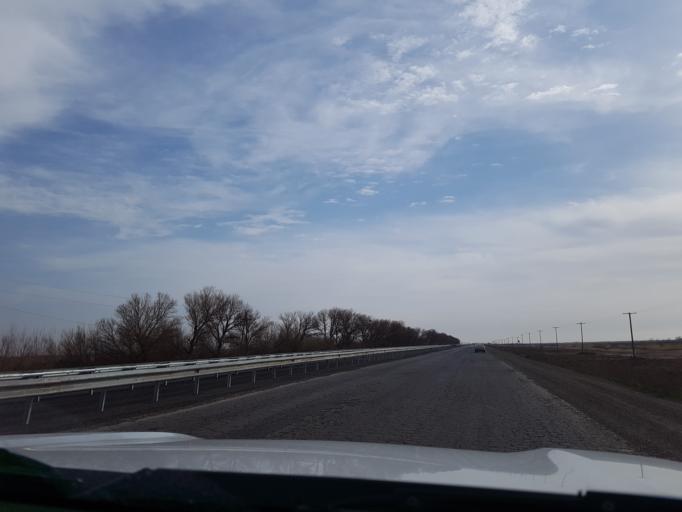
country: TM
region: Ahal
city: Tejen
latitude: 37.2290
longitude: 61.0151
